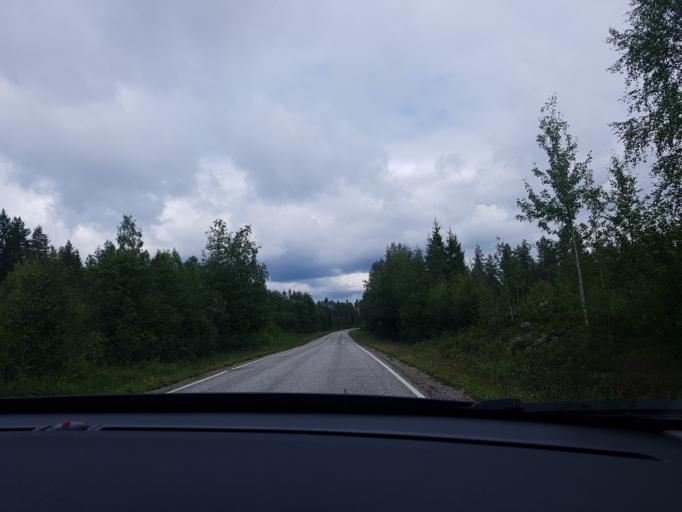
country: FI
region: Kainuu
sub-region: Kehys-Kainuu
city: Kuhmo
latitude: 64.2178
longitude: 29.4484
